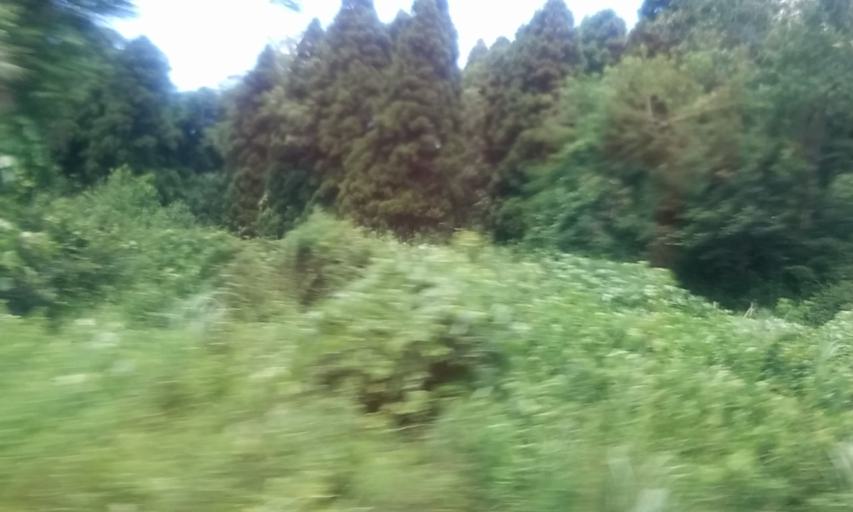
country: JP
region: Chiba
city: Chiba
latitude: 35.5646
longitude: 140.1595
